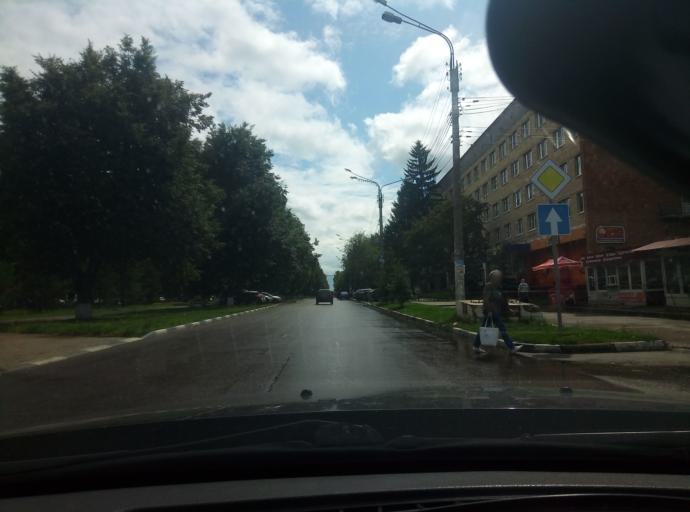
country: RU
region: Tula
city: Novomoskovsk
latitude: 54.0179
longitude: 38.2961
